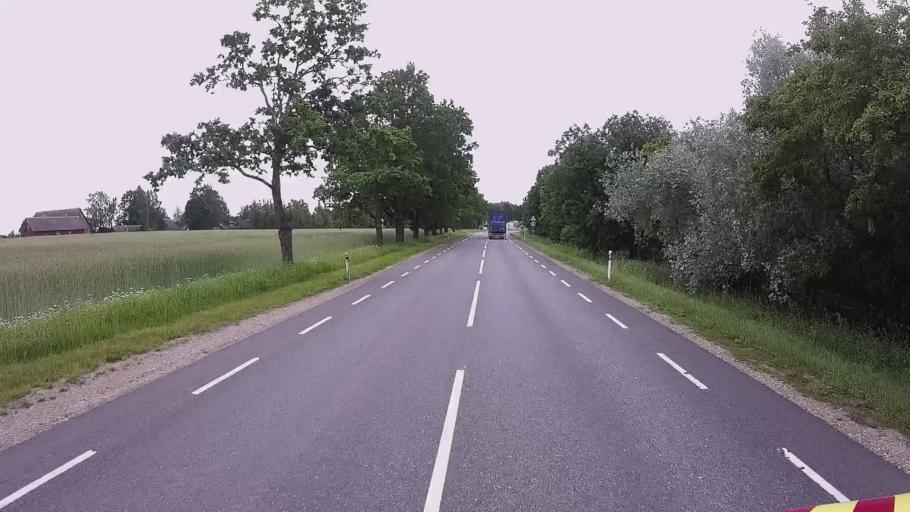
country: EE
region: Viljandimaa
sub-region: Karksi vald
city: Karksi-Nuia
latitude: 58.1220
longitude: 25.5826
